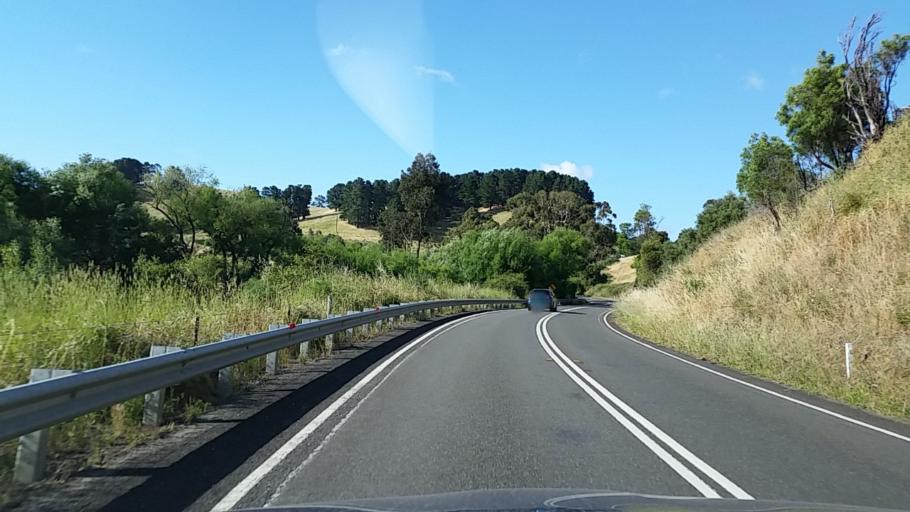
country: AU
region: South Australia
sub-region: Mount Barker
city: Meadows
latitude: -35.2389
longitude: 138.7651
